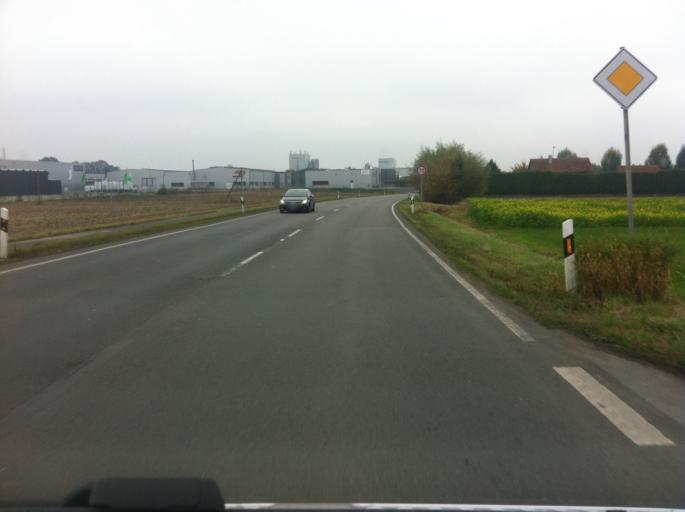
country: DE
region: North Rhine-Westphalia
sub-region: Regierungsbezirk Munster
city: Sudlohn
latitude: 51.9398
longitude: 6.8206
